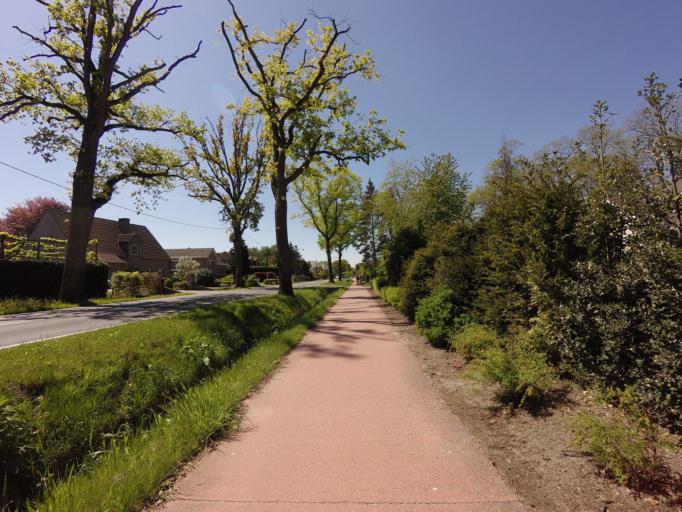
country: BE
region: Flanders
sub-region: Provincie Antwerpen
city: Essen
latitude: 51.4554
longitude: 4.4353
